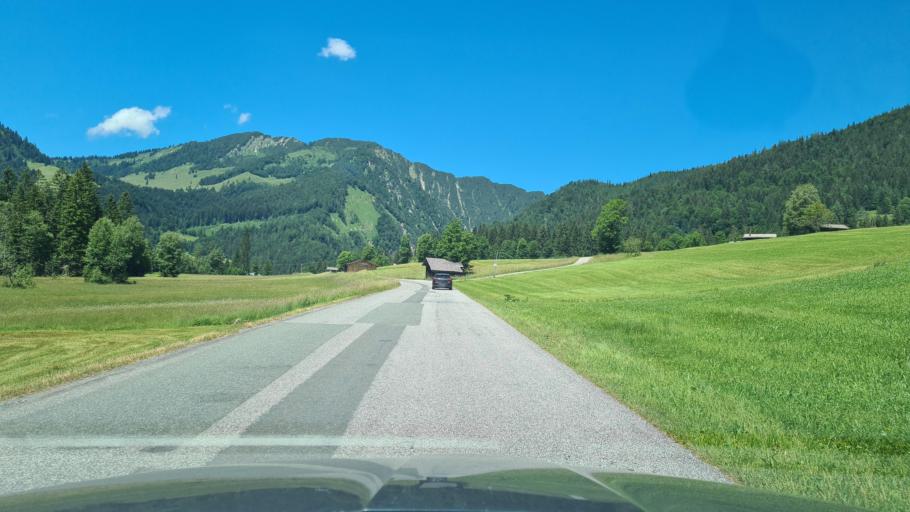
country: AT
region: Salzburg
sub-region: Politischer Bezirk Zell am See
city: Unken
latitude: 47.6588
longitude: 12.6668
